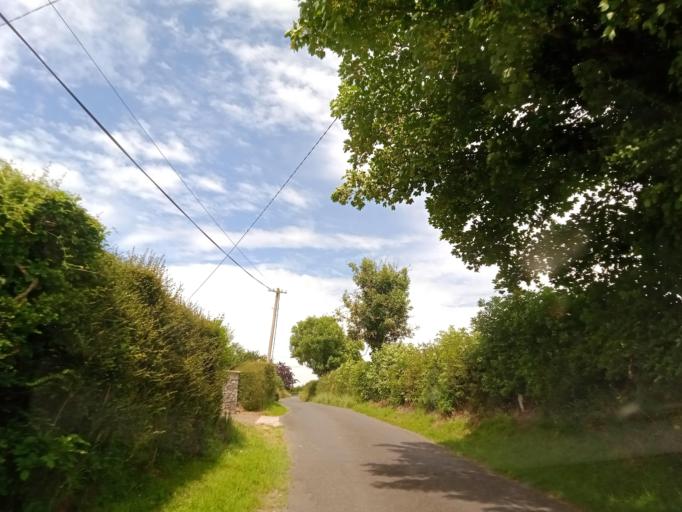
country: IE
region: Leinster
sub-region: Kilkenny
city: Thomastown
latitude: 52.5648
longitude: -7.1246
